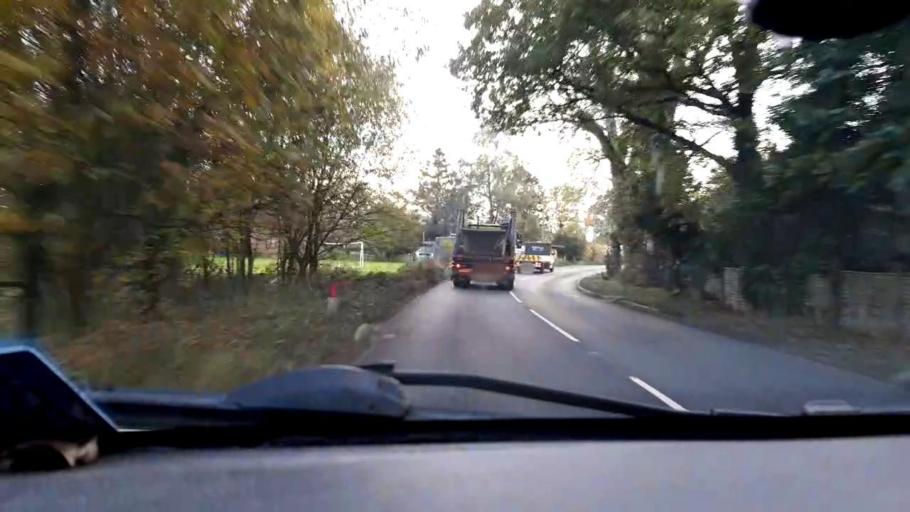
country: GB
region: England
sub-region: Norfolk
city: Mattishall
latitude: 52.6869
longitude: 1.1021
